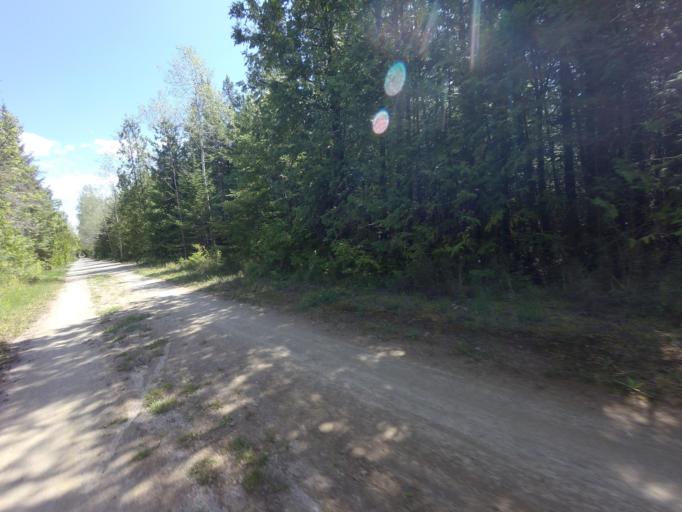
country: CA
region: Ontario
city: Orangeville
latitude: 43.7780
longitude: -80.1196
